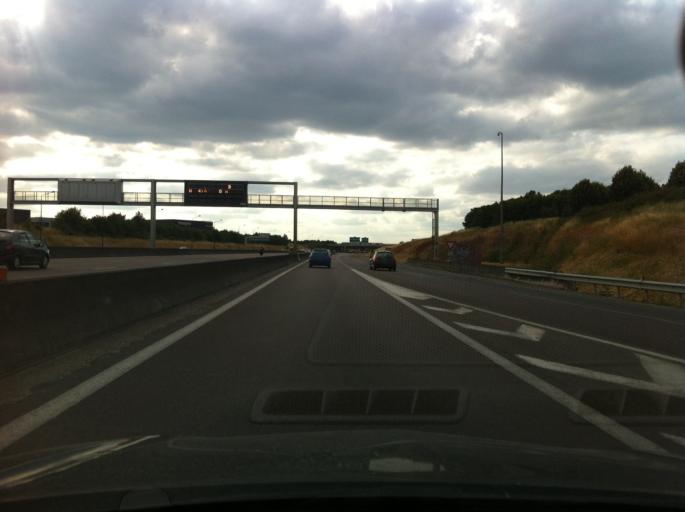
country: FR
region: Ile-de-France
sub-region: Departement de Seine-et-Marne
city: Lieusaint
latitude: 48.6205
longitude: 2.5491
